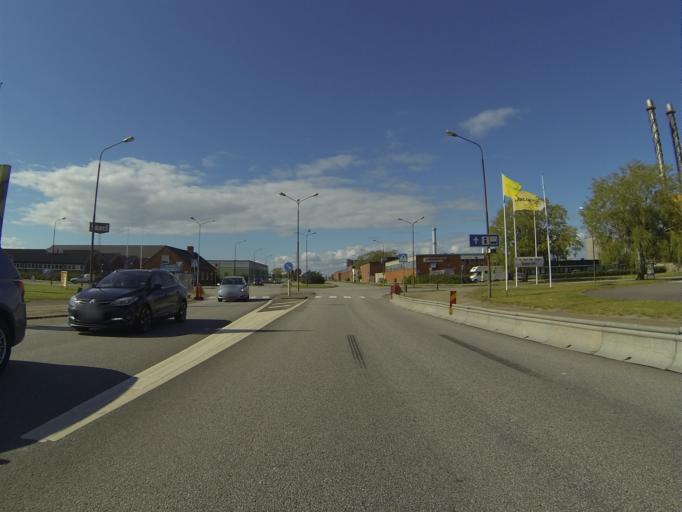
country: SE
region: Skane
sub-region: Burlovs Kommun
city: Arloev
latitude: 55.6190
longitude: 13.0387
